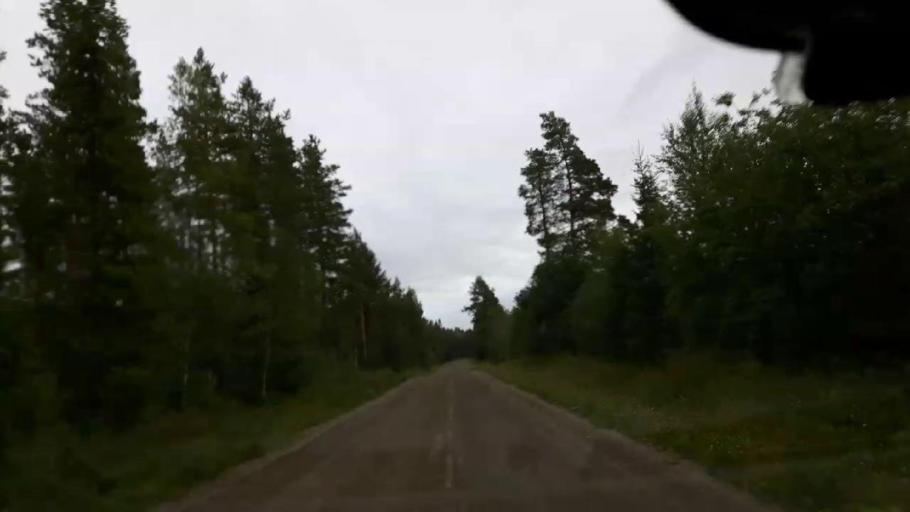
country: SE
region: Jaemtland
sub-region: Braecke Kommun
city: Braecke
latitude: 62.9497
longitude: 15.4392
